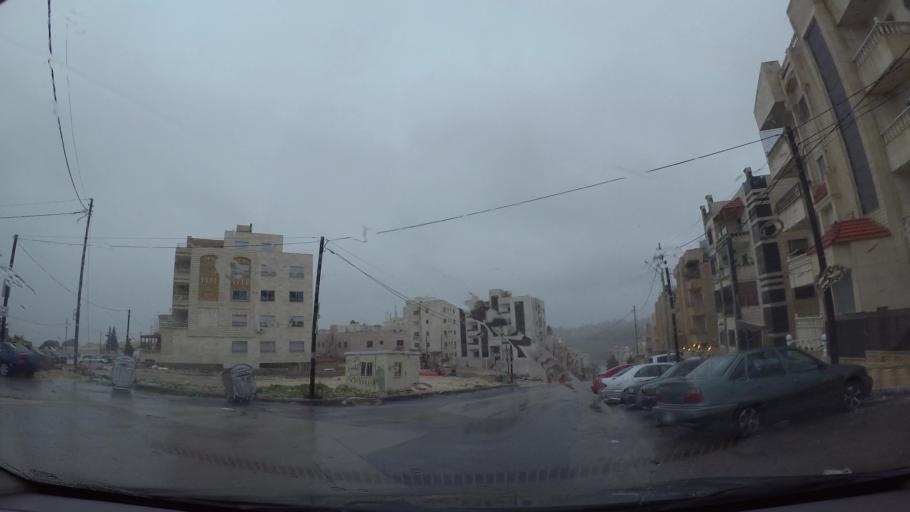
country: JO
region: Amman
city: Al Jubayhah
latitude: 32.0148
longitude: 35.8930
